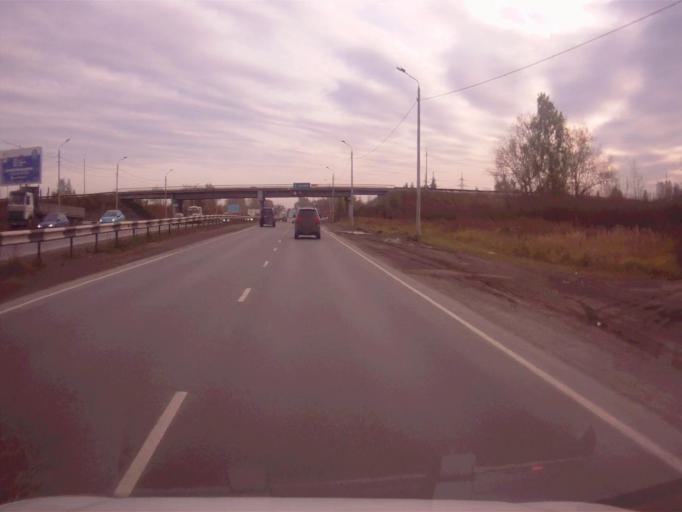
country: RU
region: Chelyabinsk
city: Novosineglazovskiy
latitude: 55.0632
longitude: 61.3988
